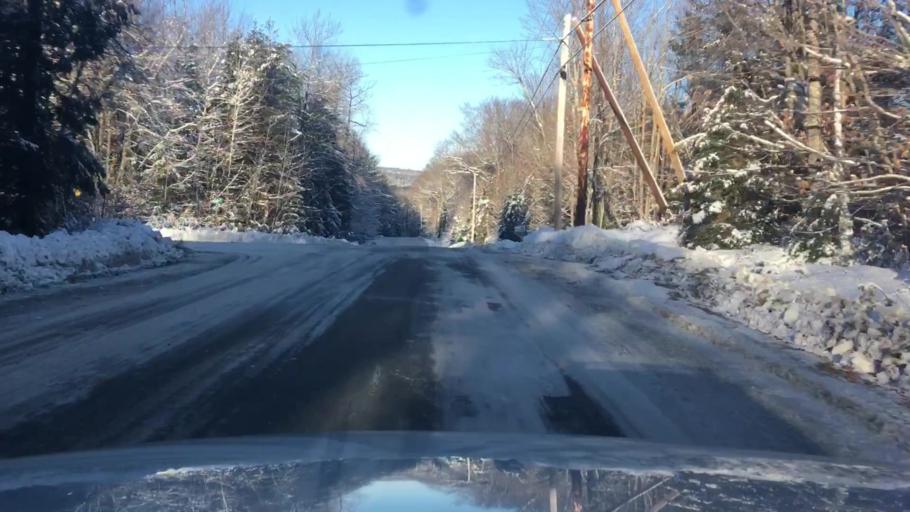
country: US
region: Maine
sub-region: Kennebec County
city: Belgrade
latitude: 44.4241
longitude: -69.8886
